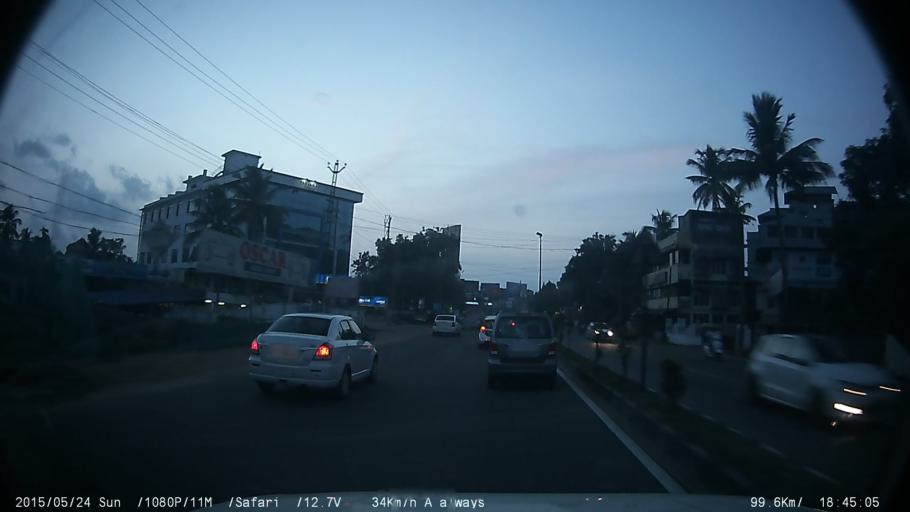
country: IN
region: Kerala
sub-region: Ernakulam
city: Aluva
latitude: 10.1205
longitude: 76.3422
